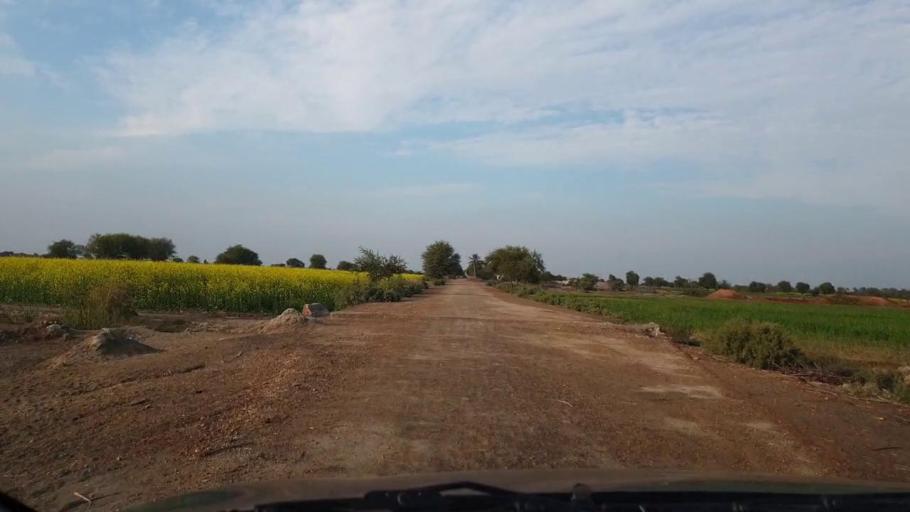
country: PK
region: Sindh
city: Jhol
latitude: 25.9751
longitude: 68.8737
